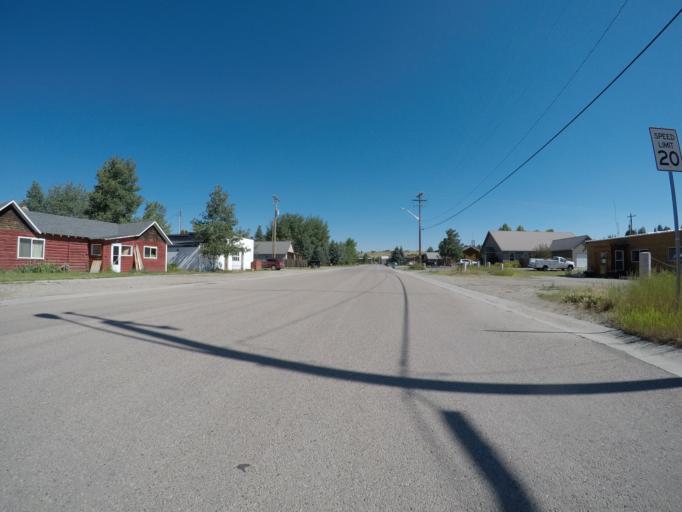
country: US
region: Wyoming
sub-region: Sublette County
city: Pinedale
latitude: 42.8676
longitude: -109.8583
